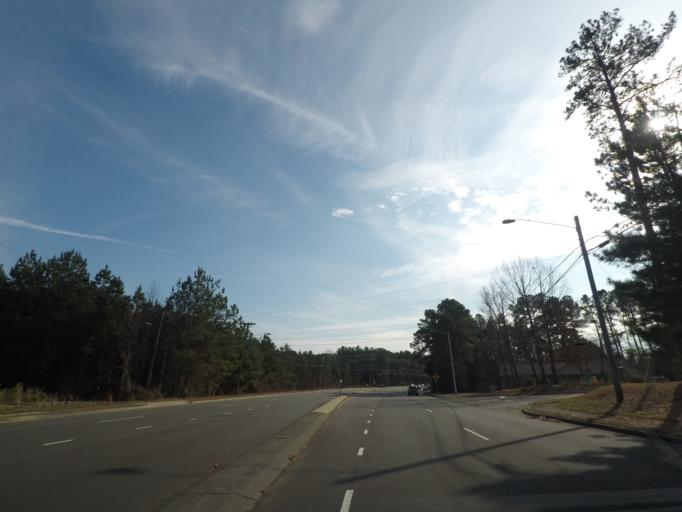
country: US
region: North Carolina
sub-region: Durham County
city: Durham
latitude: 36.0821
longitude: -78.9310
